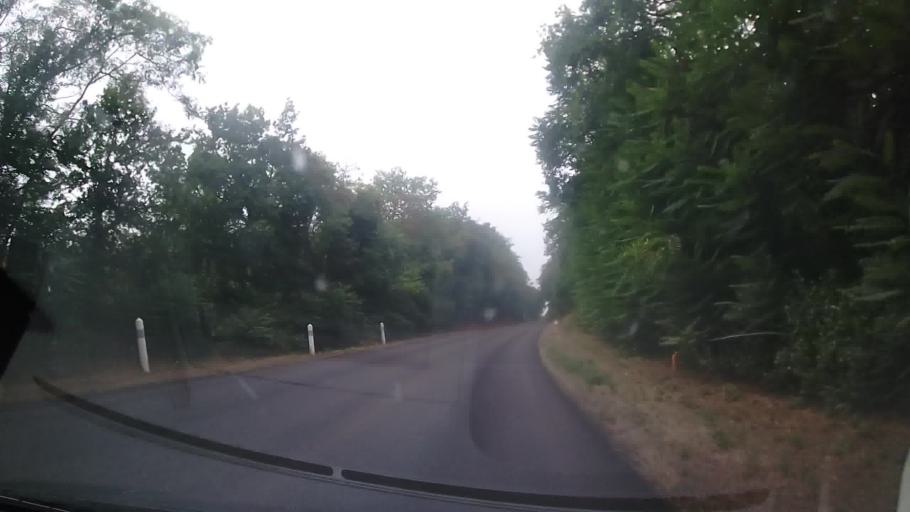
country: FR
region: Ile-de-France
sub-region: Departement de l'Essonne
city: Dourdan
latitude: 48.5390
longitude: 2.0001
